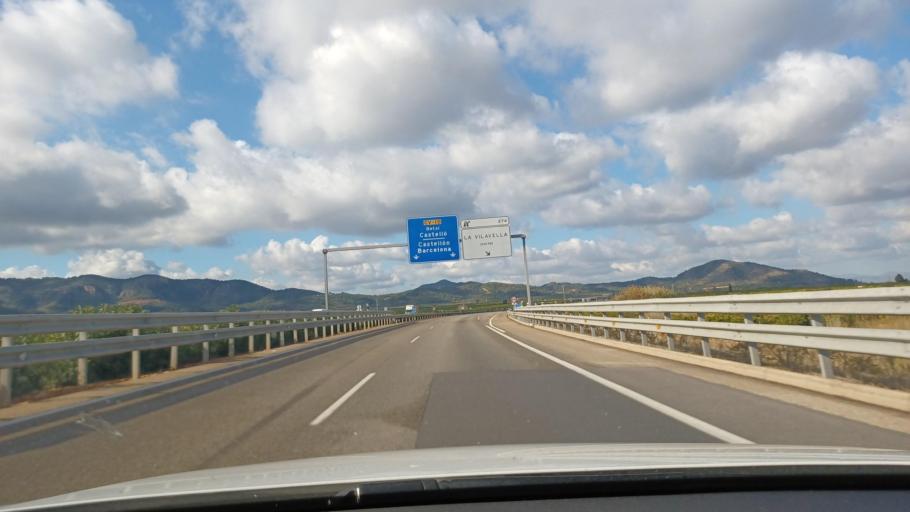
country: ES
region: Valencia
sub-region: Provincia de Castello
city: Villavieja
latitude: 39.8719
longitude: -0.1866
